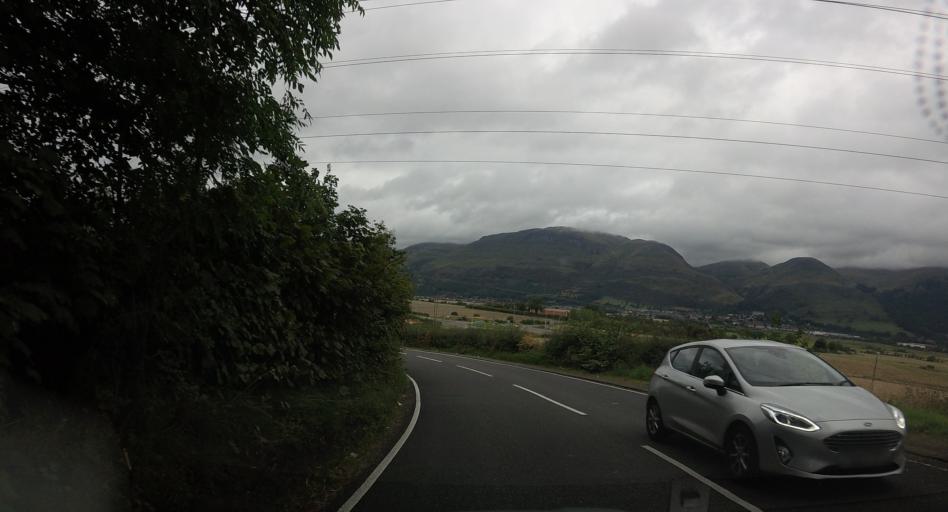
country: GB
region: Scotland
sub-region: Clackmannanshire
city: Alloa
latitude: 56.1347
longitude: -3.7951
